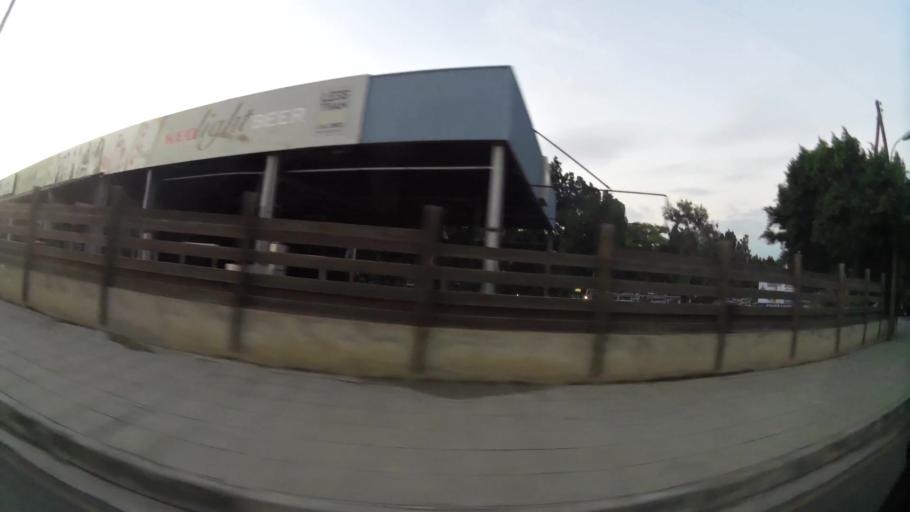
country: CY
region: Lefkosia
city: Nicosia
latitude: 35.1619
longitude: 33.3320
